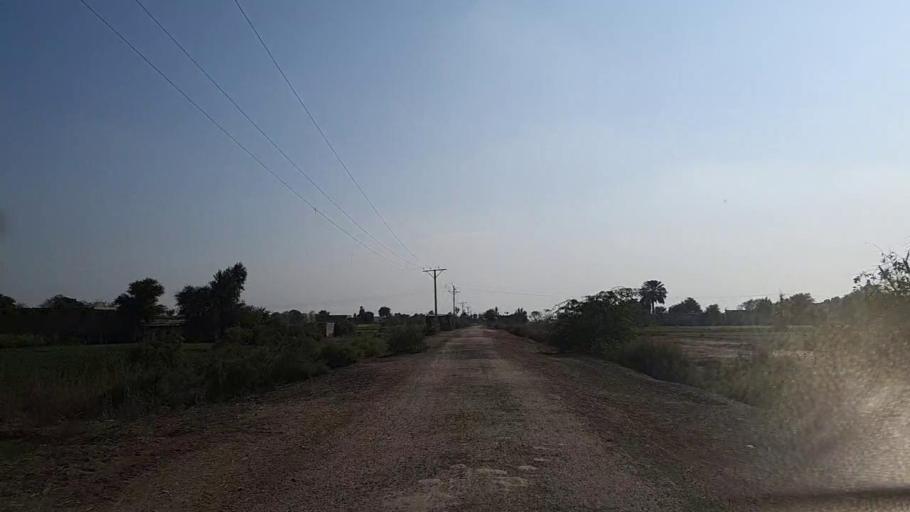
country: PK
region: Sindh
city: Jam Sahib
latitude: 26.2803
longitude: 68.6046
